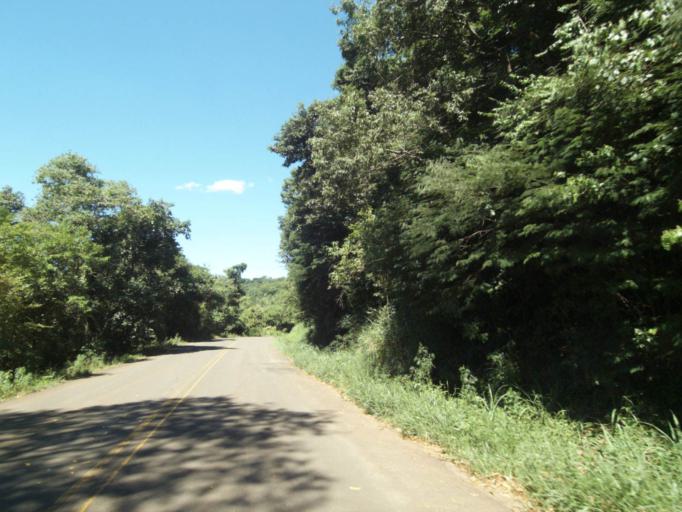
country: AR
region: Misiones
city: Bernardo de Irigoyen
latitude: -26.1877
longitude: -53.3643
